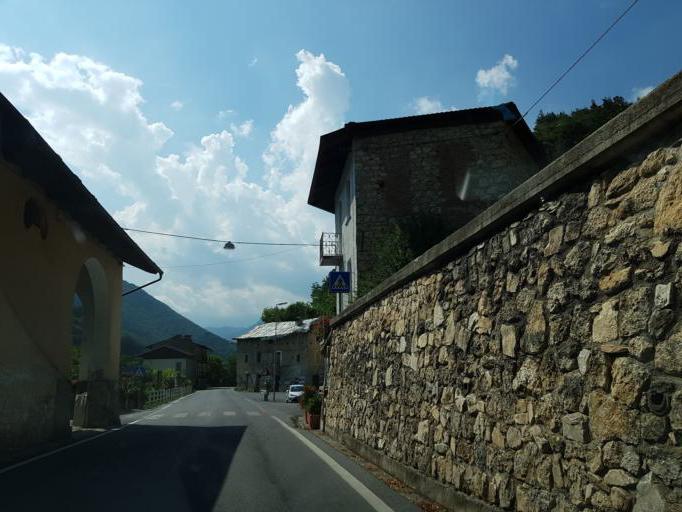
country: IT
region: Piedmont
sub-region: Provincia di Cuneo
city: Chiesa di Macra
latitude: 44.4921
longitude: 7.2169
